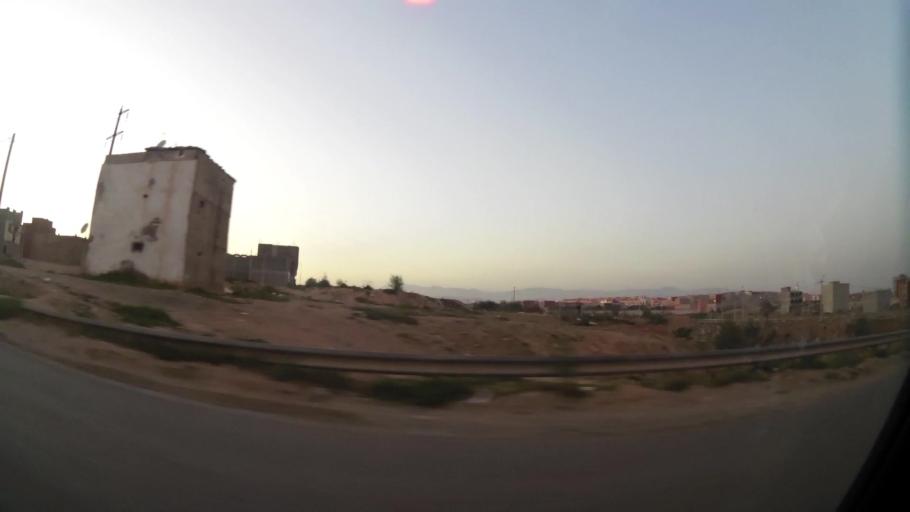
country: MA
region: Souss-Massa-Draa
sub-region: Inezgane-Ait Mellou
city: Inezgane
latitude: 30.3760
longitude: -9.4884
